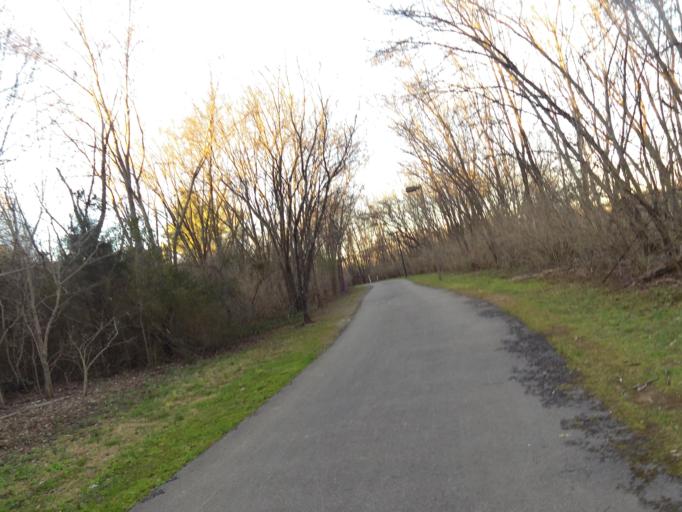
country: US
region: Tennessee
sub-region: Blount County
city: Maryville
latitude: 35.7657
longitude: -83.9816
